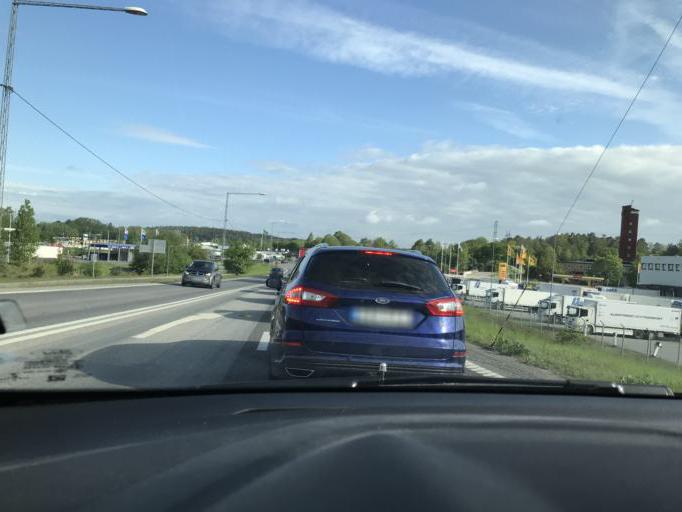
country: SE
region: Stockholm
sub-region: Botkyrka Kommun
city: Tumba
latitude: 59.2128
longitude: 17.8308
